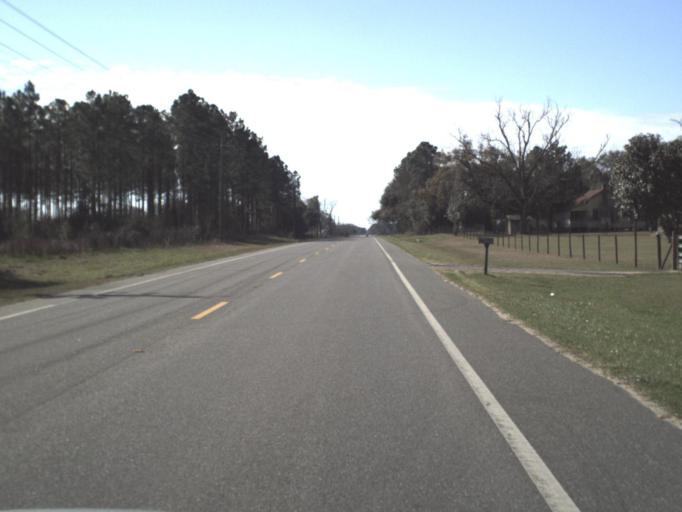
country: US
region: Florida
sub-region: Jackson County
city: Malone
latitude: 30.9127
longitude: -85.1609
